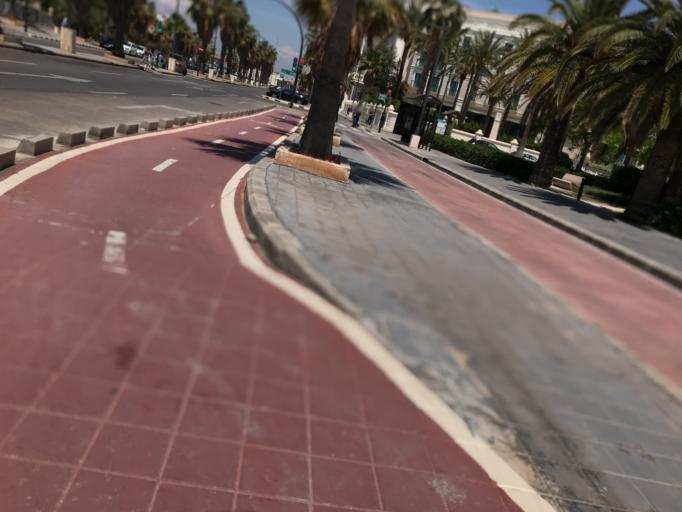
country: ES
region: Valencia
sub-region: Provincia de Valencia
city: Alboraya
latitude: 39.4651
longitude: -0.3247
